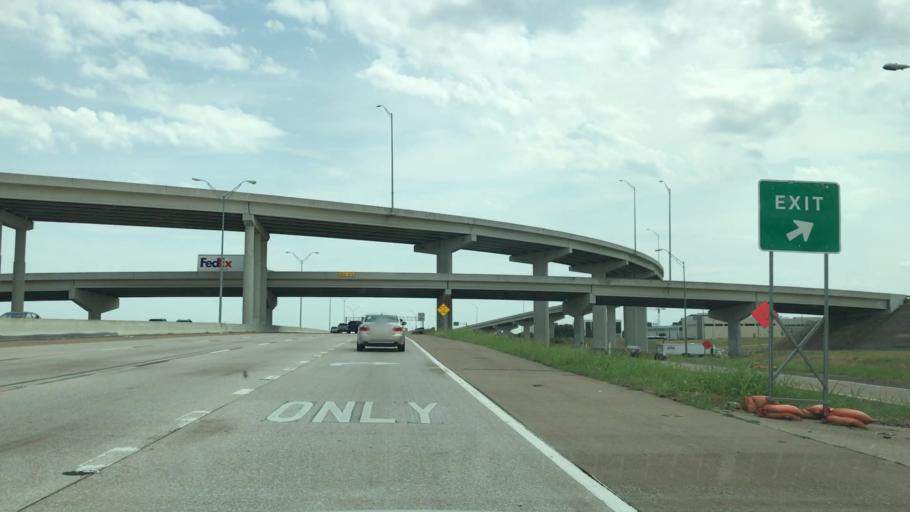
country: US
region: Texas
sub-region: Tarrant County
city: Euless
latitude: 32.8410
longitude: -97.0611
